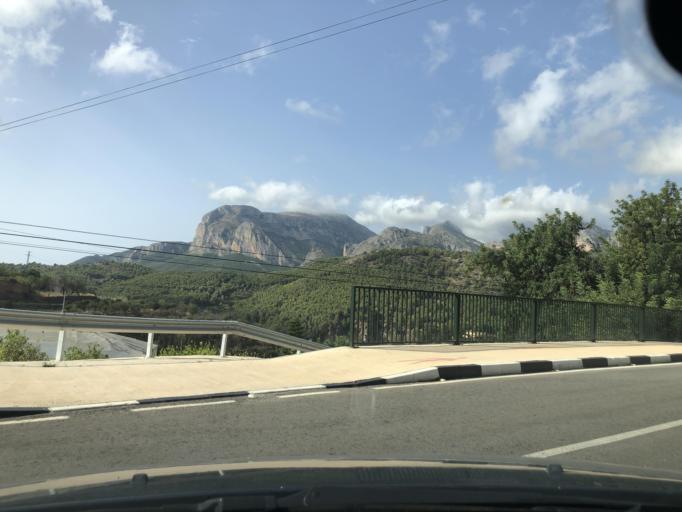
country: ES
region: Valencia
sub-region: Provincia de Alicante
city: Callosa d'En Sarria
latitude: 38.6526
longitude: -0.1309
